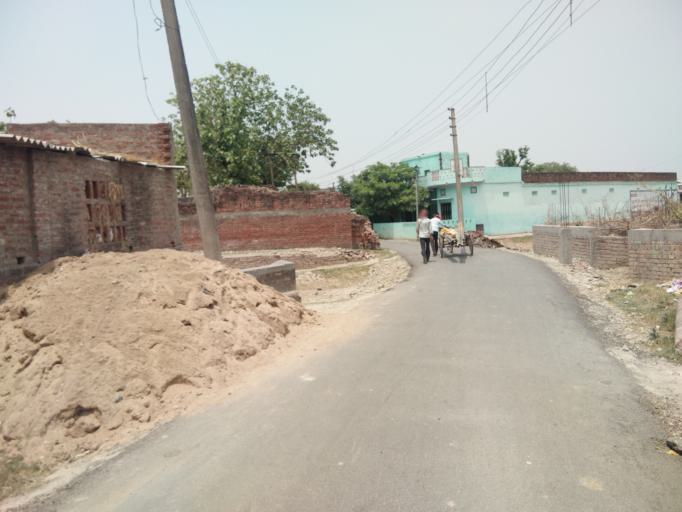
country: IN
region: Uttar Pradesh
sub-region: Ghazipur
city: Zamania
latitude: 25.4411
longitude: 83.6849
